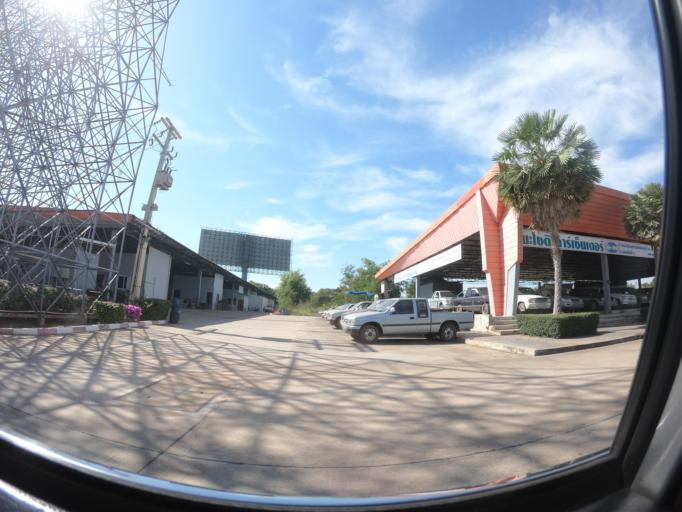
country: TH
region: Khon Kaen
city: Khon Kaen
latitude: 16.3883
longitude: 102.8103
